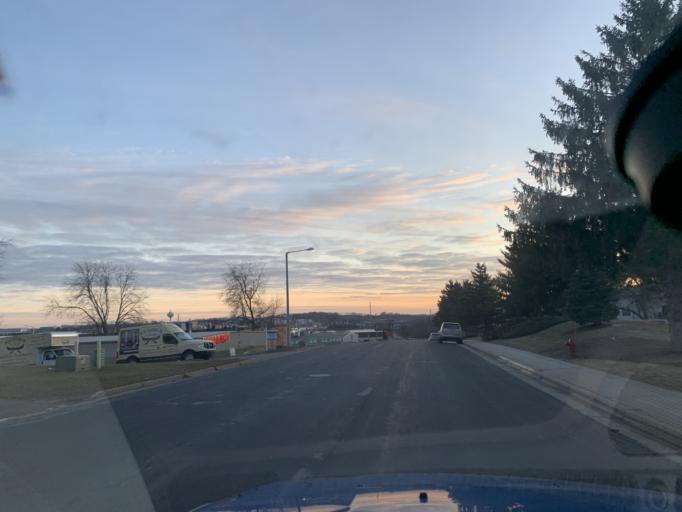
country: US
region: Wisconsin
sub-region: Dane County
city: Fitchburg
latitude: 43.0221
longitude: -89.4720
